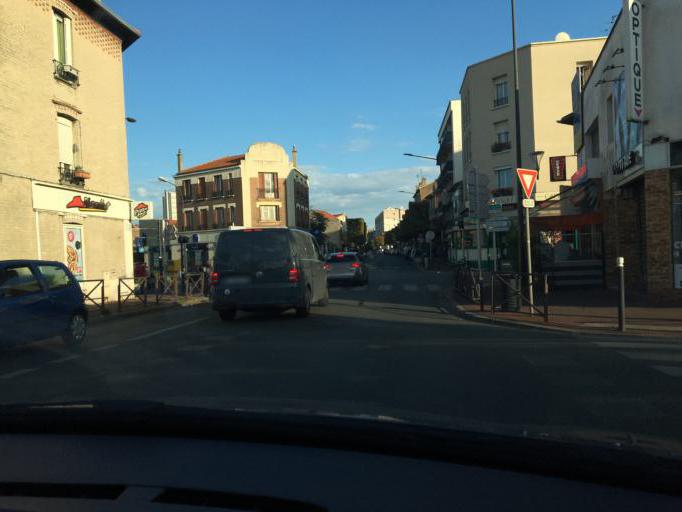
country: FR
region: Ile-de-France
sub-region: Departement du Val-de-Marne
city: Fontenay-sous-Bois
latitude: 48.8539
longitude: 2.4693
